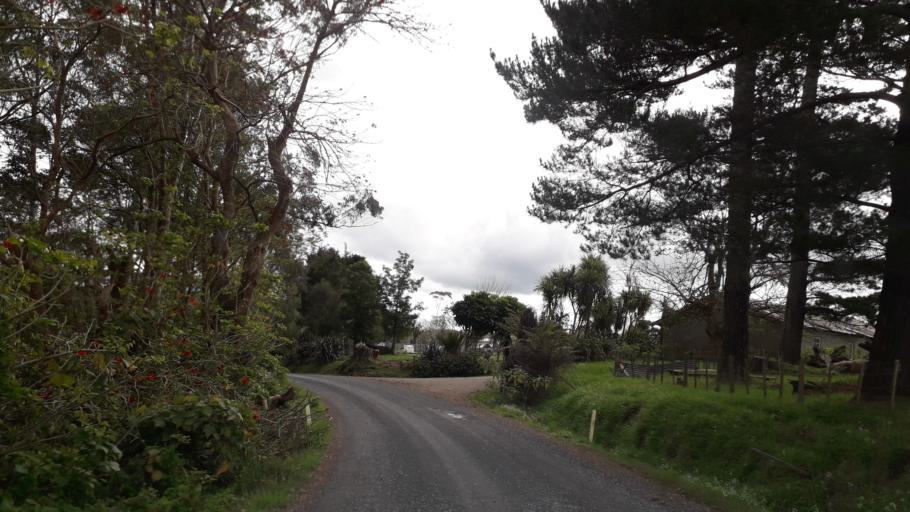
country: NZ
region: Northland
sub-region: Far North District
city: Taipa
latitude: -35.0932
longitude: 173.5234
